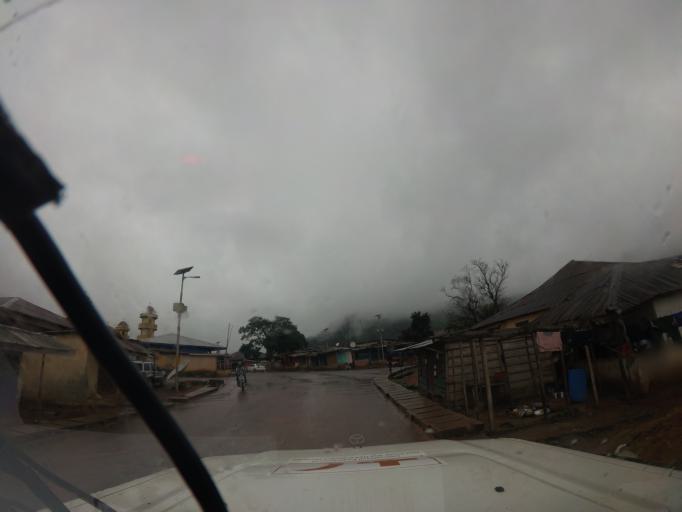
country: SL
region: Northern Province
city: Kabala
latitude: 9.5859
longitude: -11.5521
